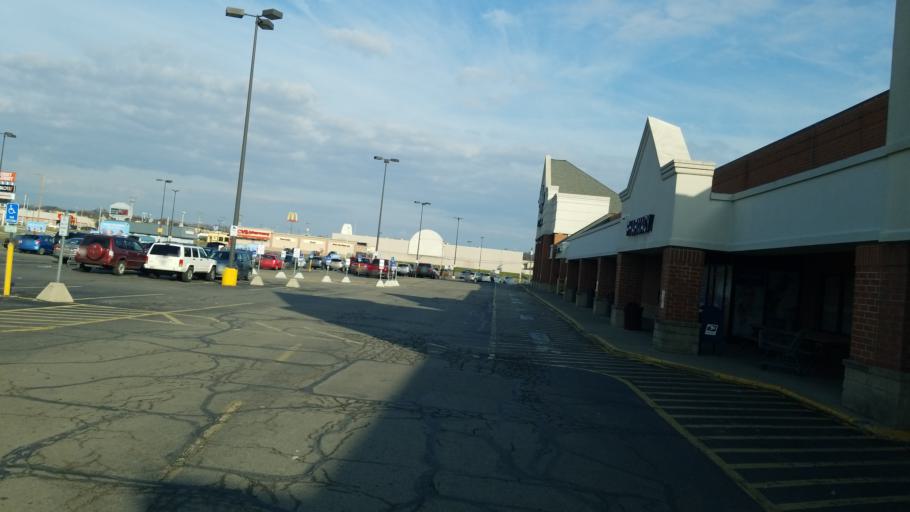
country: US
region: Ohio
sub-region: Ross County
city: Chillicothe
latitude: 39.3538
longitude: -82.9748
